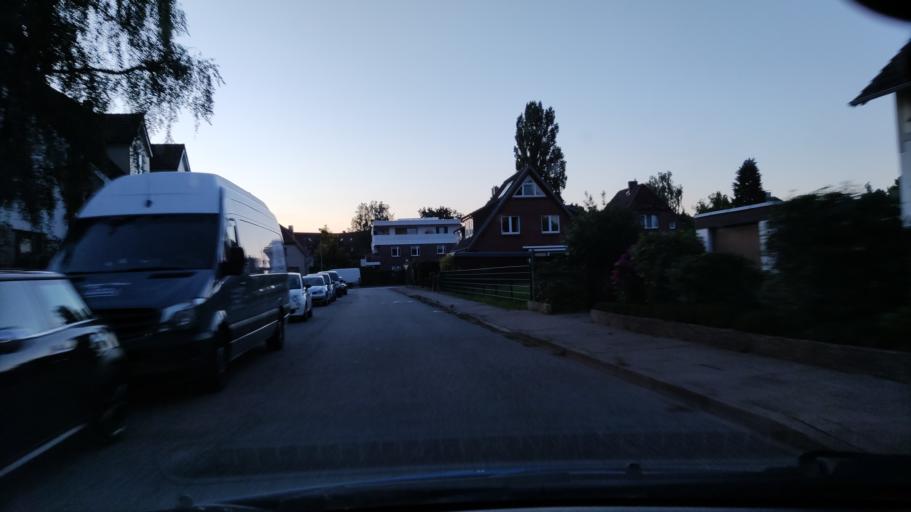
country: DE
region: Schleswig-Holstein
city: Wedel
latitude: 53.5742
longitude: 9.7113
